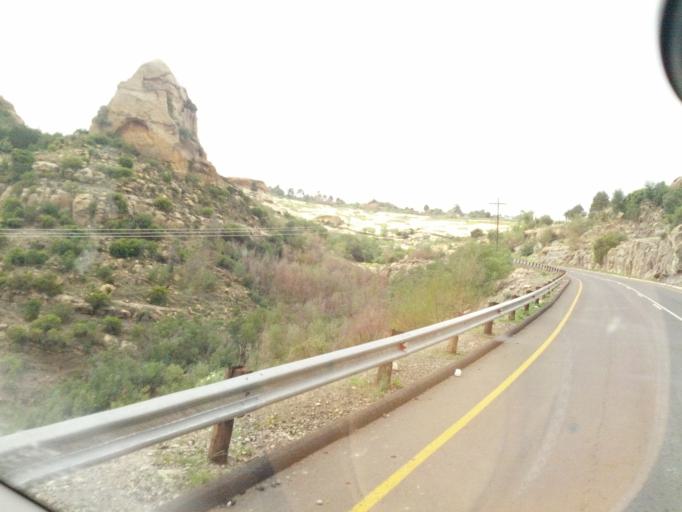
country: LS
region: Maseru
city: Nako
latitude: -29.4813
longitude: 27.7407
